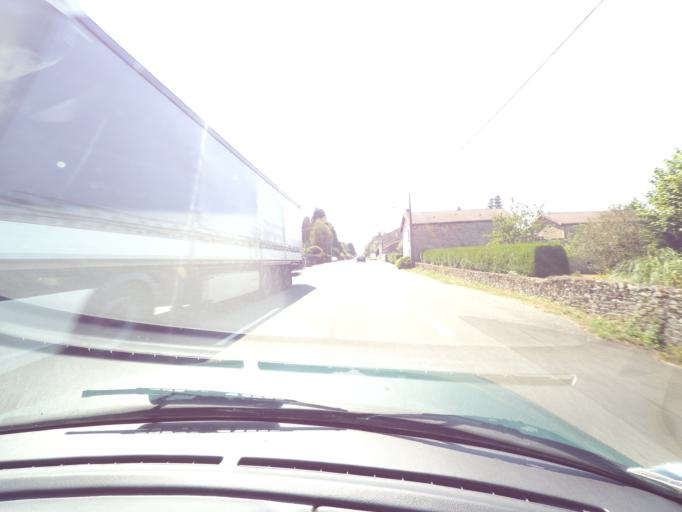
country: FR
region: Limousin
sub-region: Departement de la Haute-Vienne
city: Couzeix
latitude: 45.8965
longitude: 1.2294
